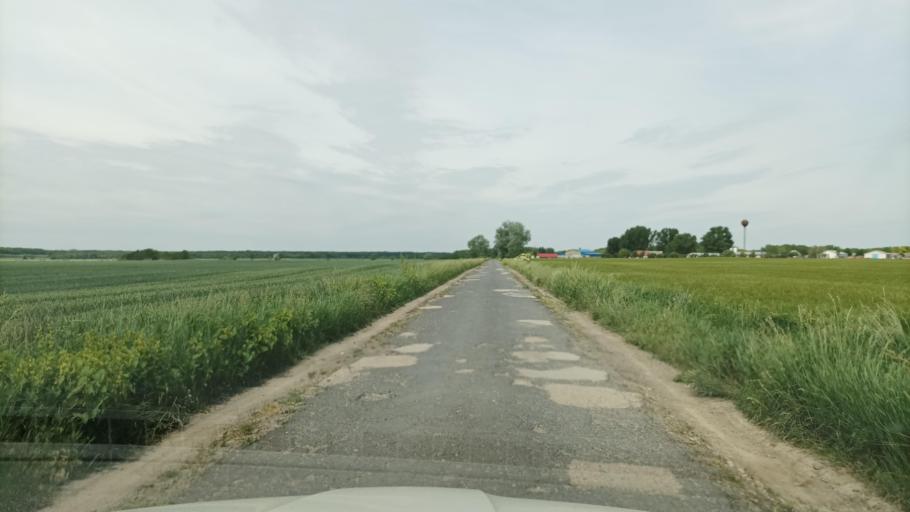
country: HU
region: Fejer
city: Racalmas
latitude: 47.0729
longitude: 18.9511
